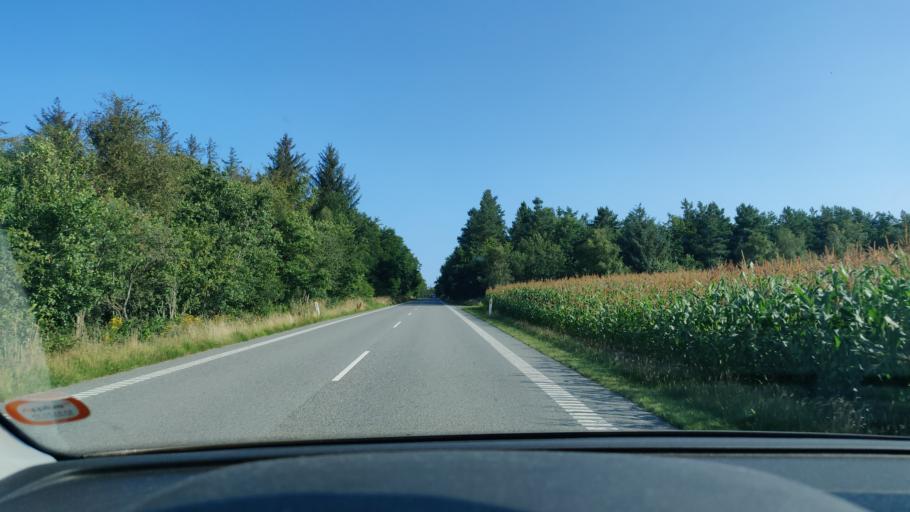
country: DK
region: North Denmark
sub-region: Jammerbugt Kommune
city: Pandrup
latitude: 57.2489
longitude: 9.6455
